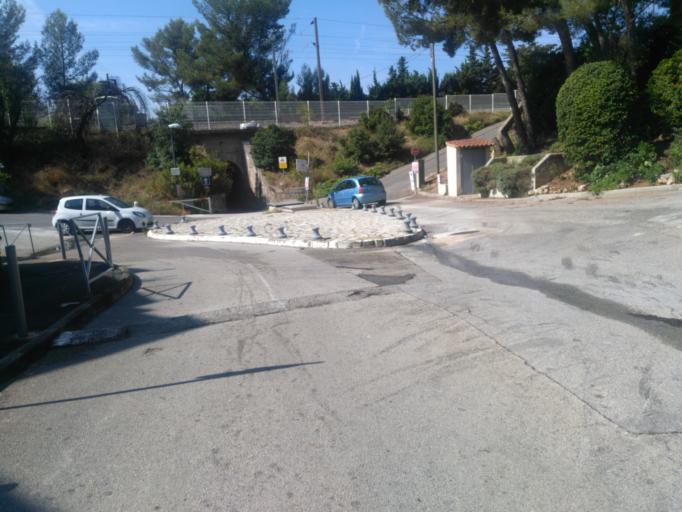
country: FR
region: Provence-Alpes-Cote d'Azur
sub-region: Departement du Var
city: Bandol
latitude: 43.1416
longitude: 5.7466
